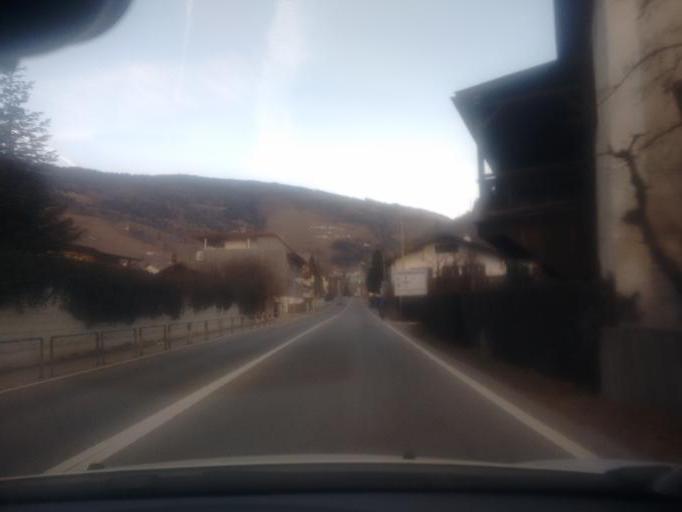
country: IT
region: Trentino-Alto Adige
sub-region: Bolzano
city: Vipiteno
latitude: 46.8960
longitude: 11.4356
